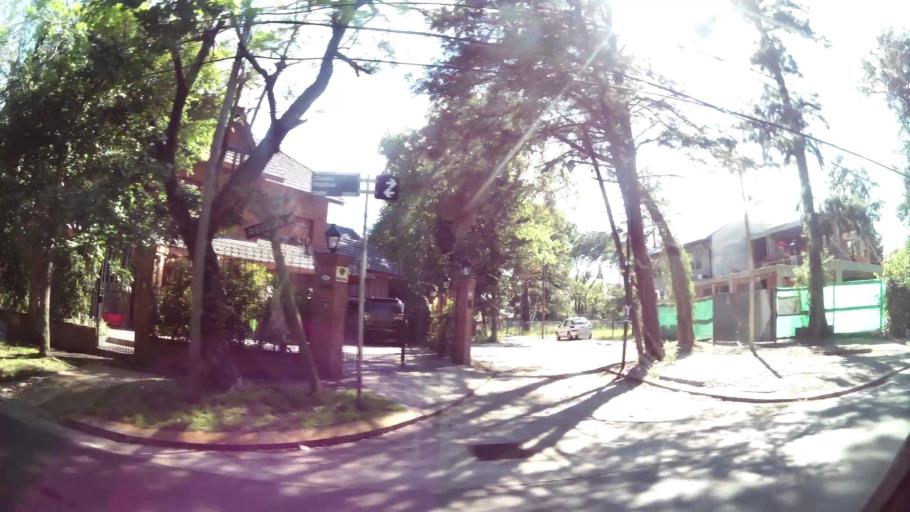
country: AR
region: Buenos Aires
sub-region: Partido de Tigre
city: Tigre
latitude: -34.4795
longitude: -58.5765
